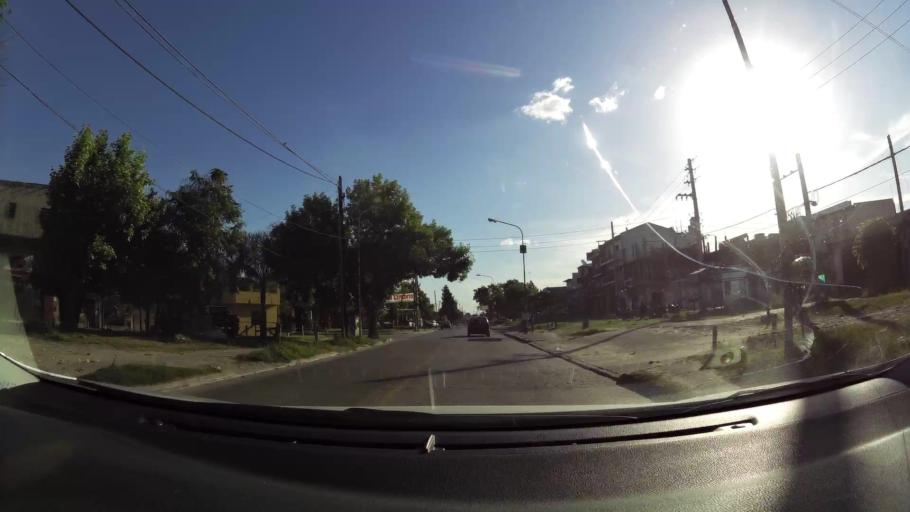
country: AR
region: Buenos Aires F.D.
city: Villa Lugano
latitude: -34.7009
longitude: -58.4728
